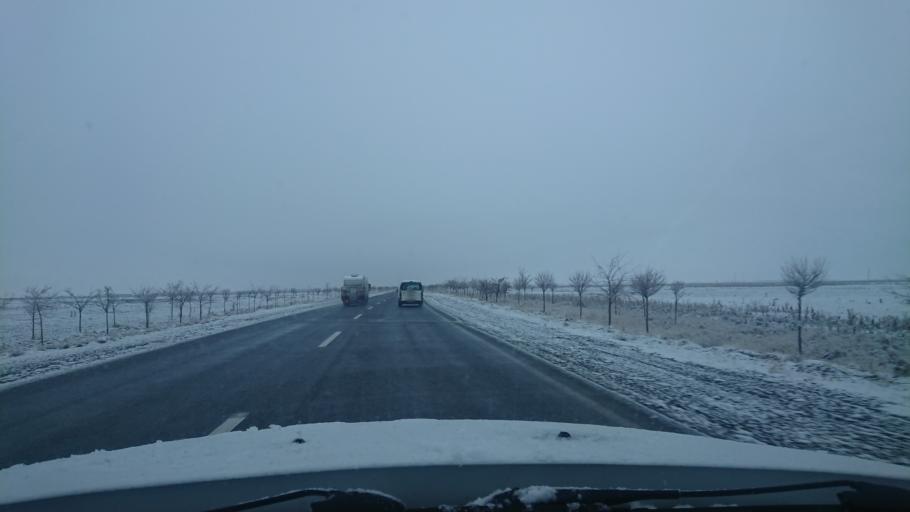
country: TR
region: Aksaray
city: Yesilova
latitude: 38.3115
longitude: 33.7537
